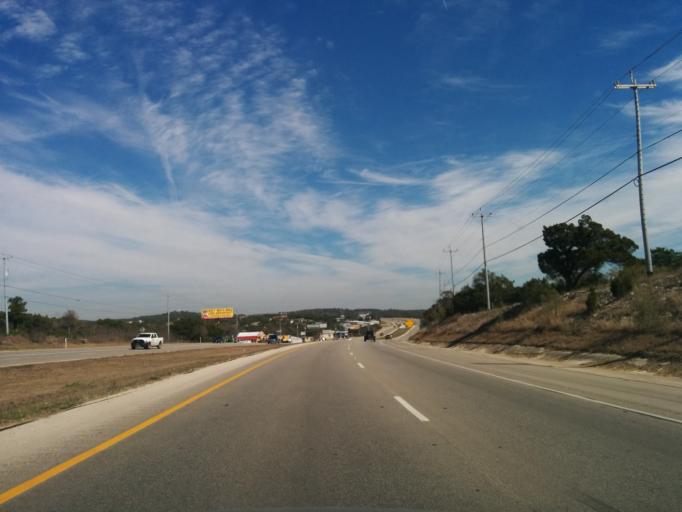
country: US
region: Texas
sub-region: Comal County
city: Bulverde
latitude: 29.7384
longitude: -98.4383
